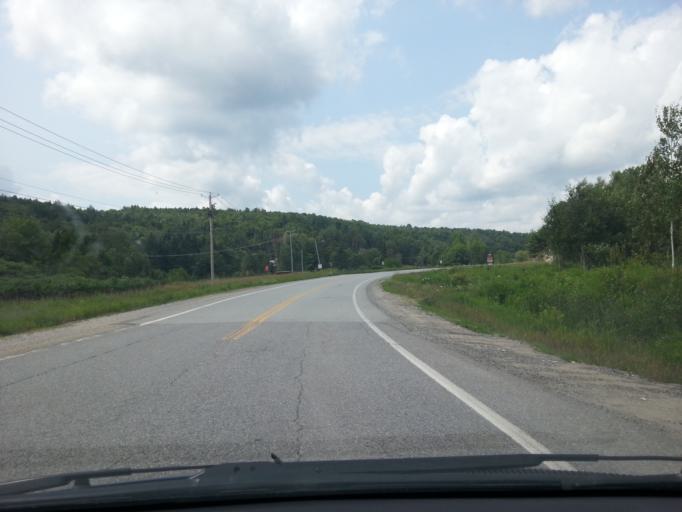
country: CA
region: Quebec
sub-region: Outaouais
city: Val-des-Monts
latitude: 45.6526
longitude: -75.6847
